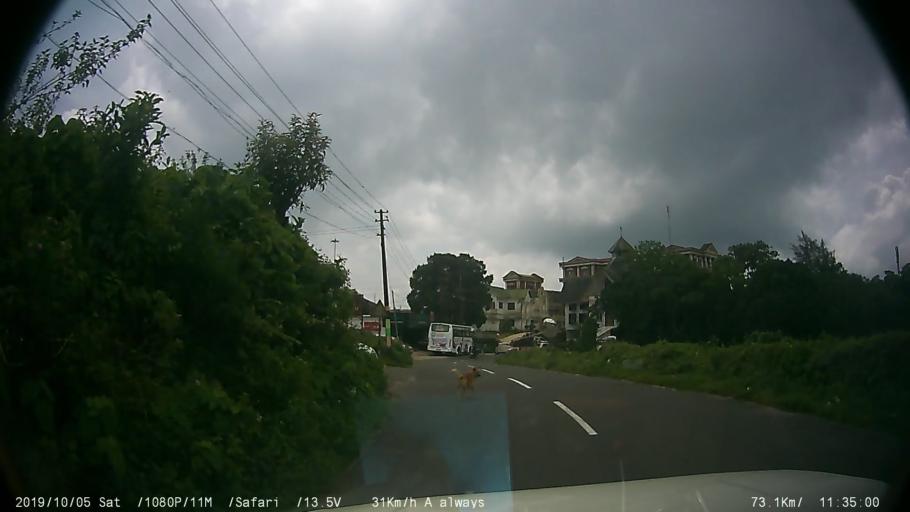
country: IN
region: Kerala
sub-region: Kottayam
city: Erattupetta
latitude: 9.5849
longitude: 76.9706
